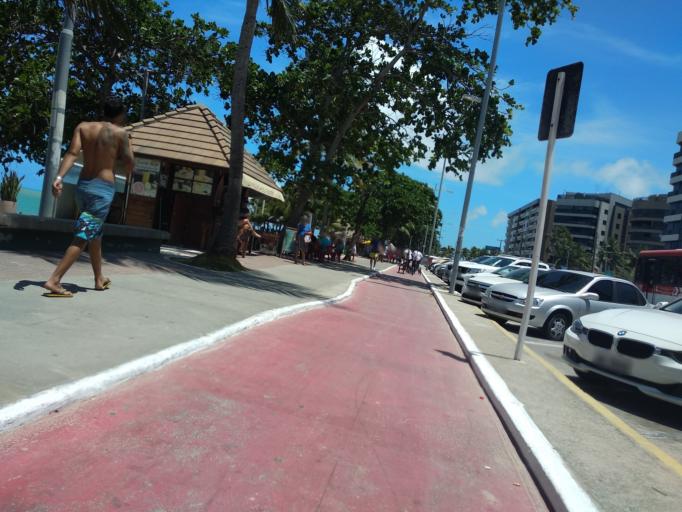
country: BR
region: Alagoas
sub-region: Maceio
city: Maceio
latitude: -9.6615
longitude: -35.6967
